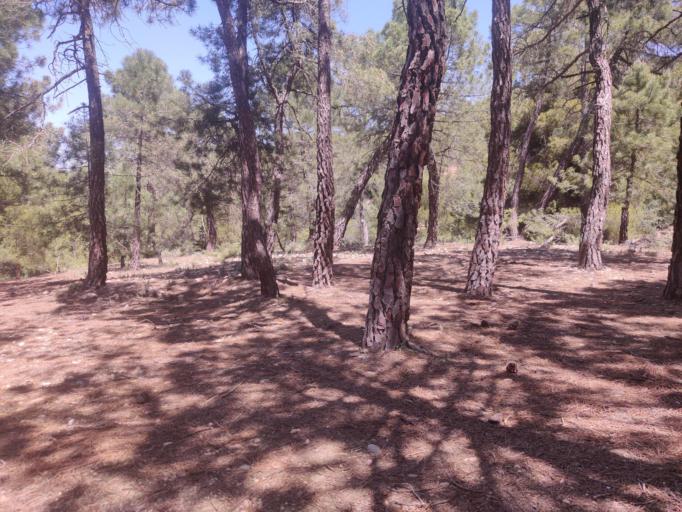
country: ES
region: Castille-La Mancha
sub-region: Provincia de Albacete
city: Penas de San Pedro
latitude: 38.7415
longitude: -2.0253
